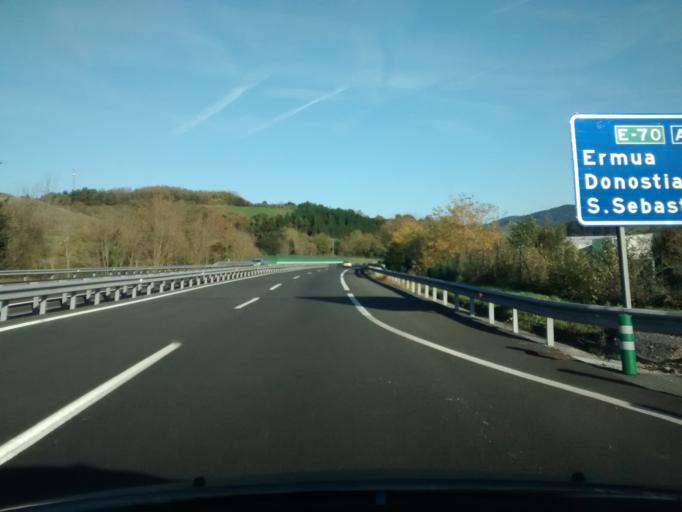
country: ES
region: Basque Country
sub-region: Bizkaia
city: Berriz
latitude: 43.1689
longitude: -2.5889
